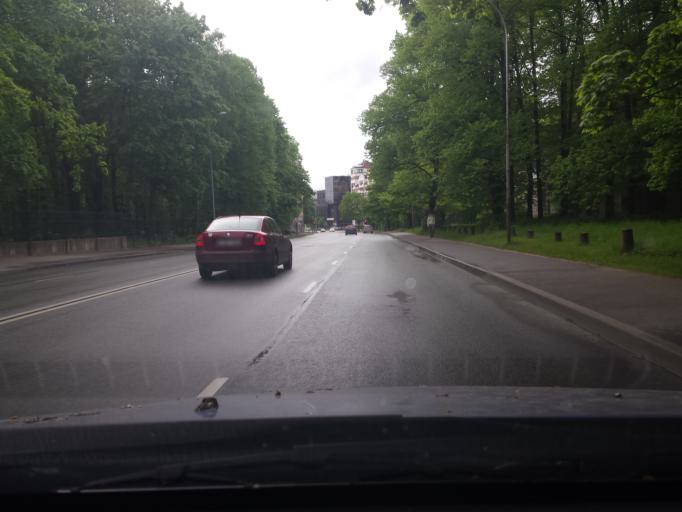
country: LV
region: Riga
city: Riga
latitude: 56.9696
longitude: 24.1409
